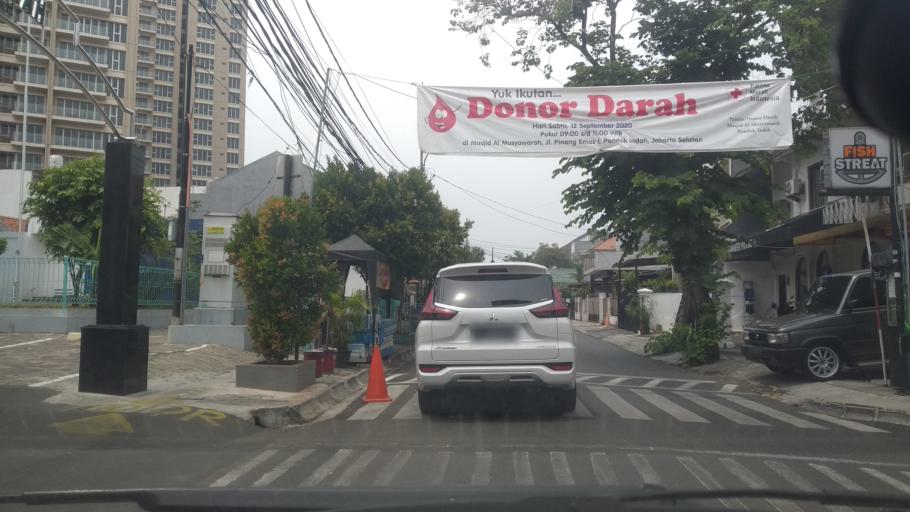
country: ID
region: Banten
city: South Tangerang
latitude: -6.2638
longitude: 106.7793
